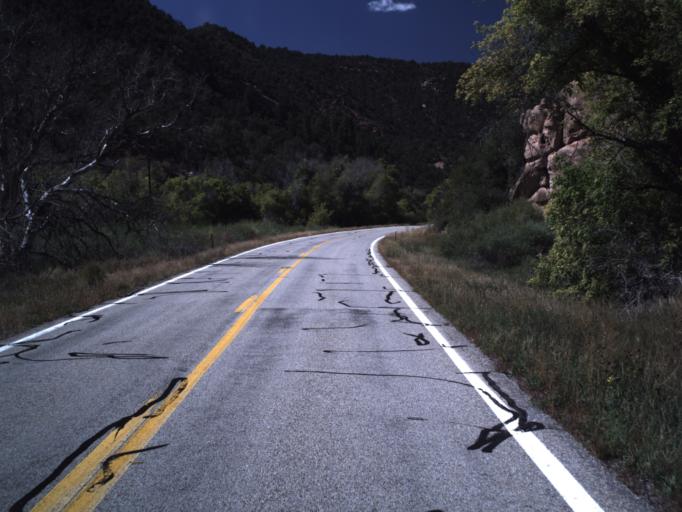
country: US
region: Utah
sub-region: San Juan County
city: Monticello
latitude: 38.3270
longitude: -109.0627
